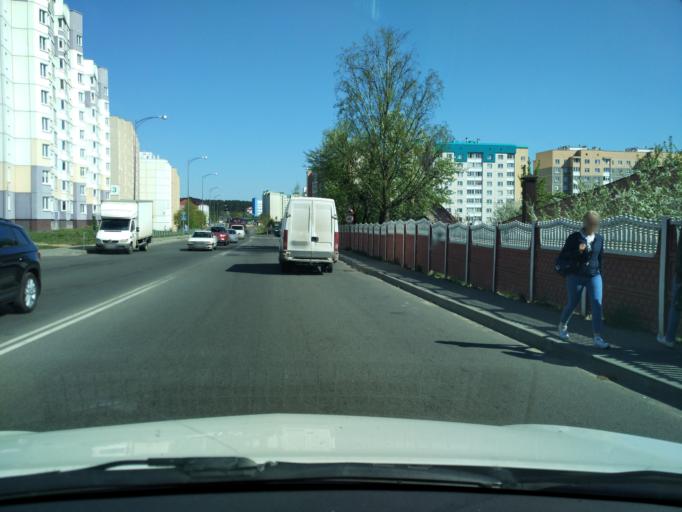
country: BY
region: Minsk
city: Borovlyany
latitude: 53.9997
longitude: 27.6771
